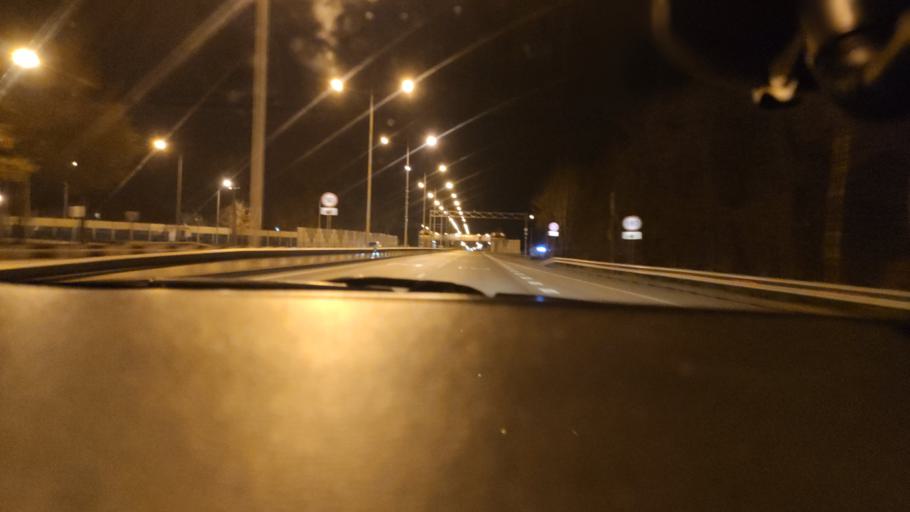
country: RU
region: Perm
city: Kondratovo
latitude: 57.9392
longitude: 56.0480
